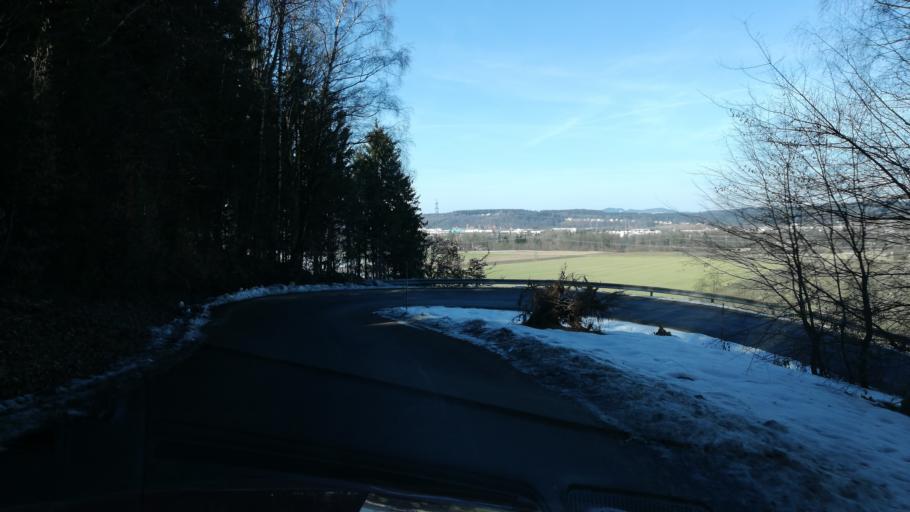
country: AT
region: Upper Austria
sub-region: Politischer Bezirk Vocklabruck
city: Vocklabruck
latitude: 47.9865
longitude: 13.6548
